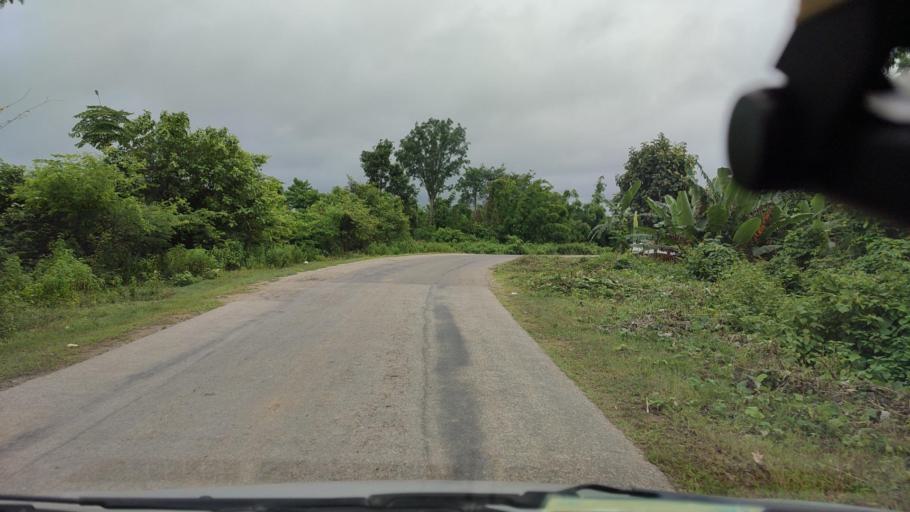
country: MM
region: Mandalay
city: Nay Pyi Taw
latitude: 19.9839
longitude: 95.9645
